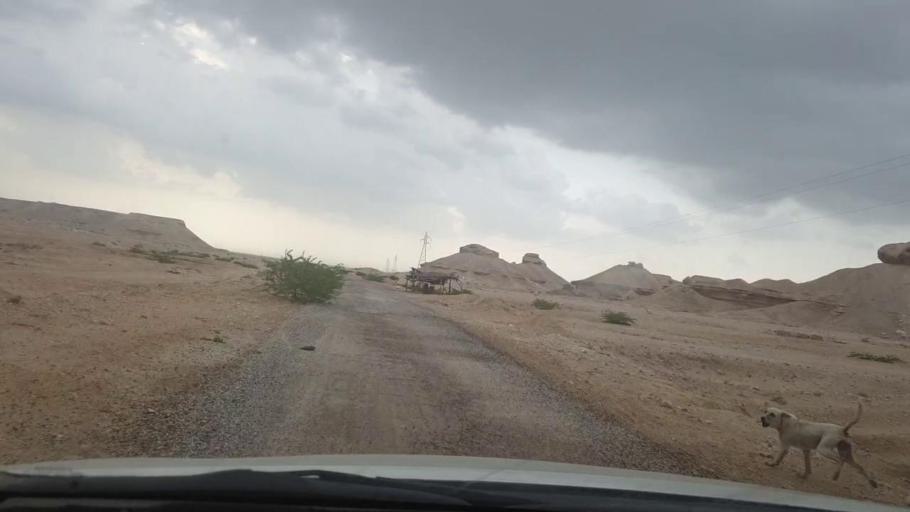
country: PK
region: Sindh
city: Khairpur
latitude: 27.4701
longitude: 68.8974
